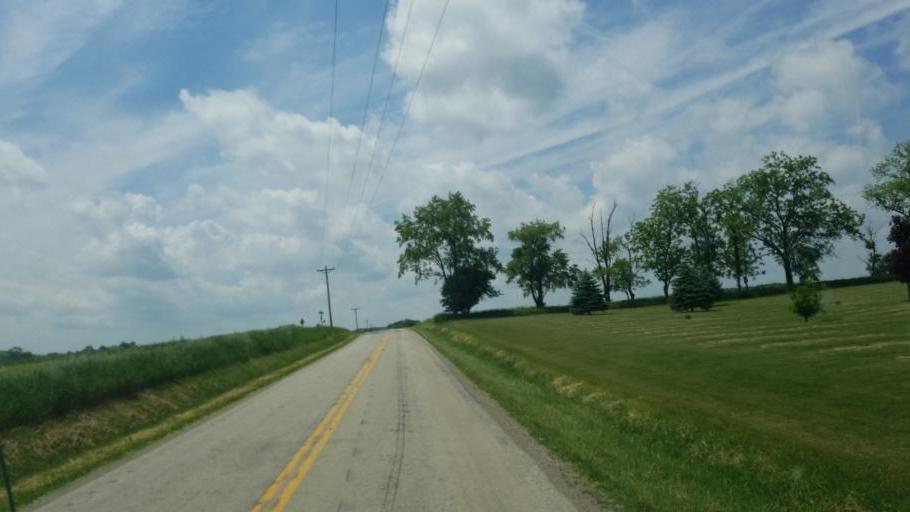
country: US
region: Ohio
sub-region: Ashland County
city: Ashland
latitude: 40.8061
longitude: -82.2393
